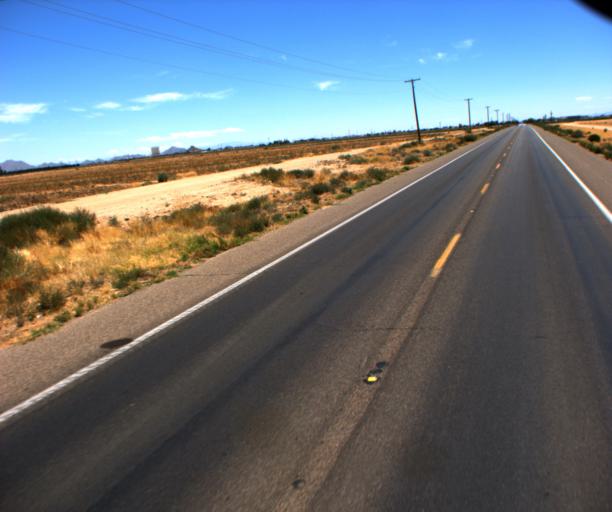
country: US
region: Arizona
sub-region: Pinal County
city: Casa Grande
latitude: 32.8794
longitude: -111.8162
